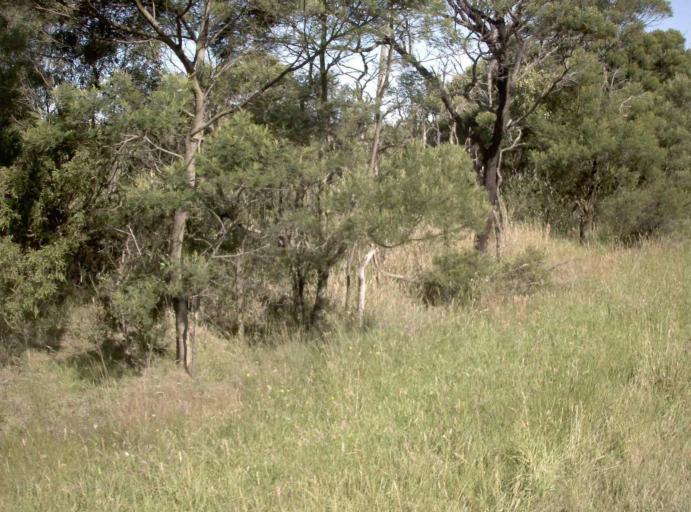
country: AU
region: Victoria
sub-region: Latrobe
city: Traralgon
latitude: -38.6225
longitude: 146.6730
